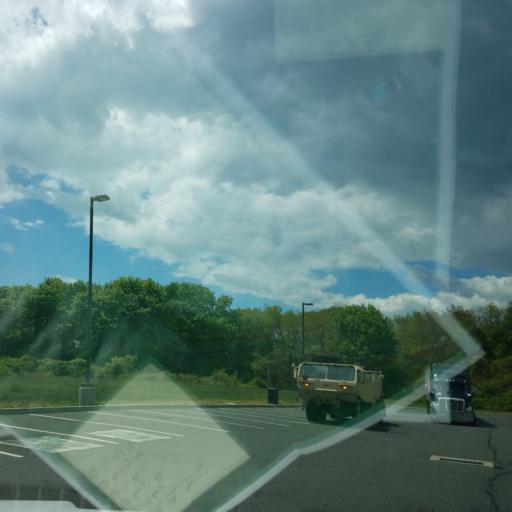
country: US
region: Connecticut
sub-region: New Haven County
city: Madison
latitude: 41.2901
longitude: -72.5802
